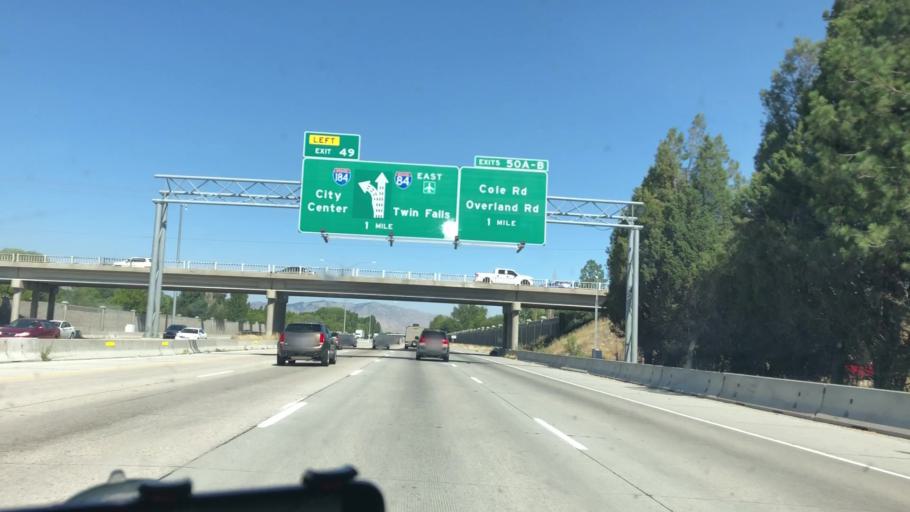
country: US
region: Idaho
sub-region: Ada County
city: Meridian
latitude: 43.5972
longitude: -116.3151
